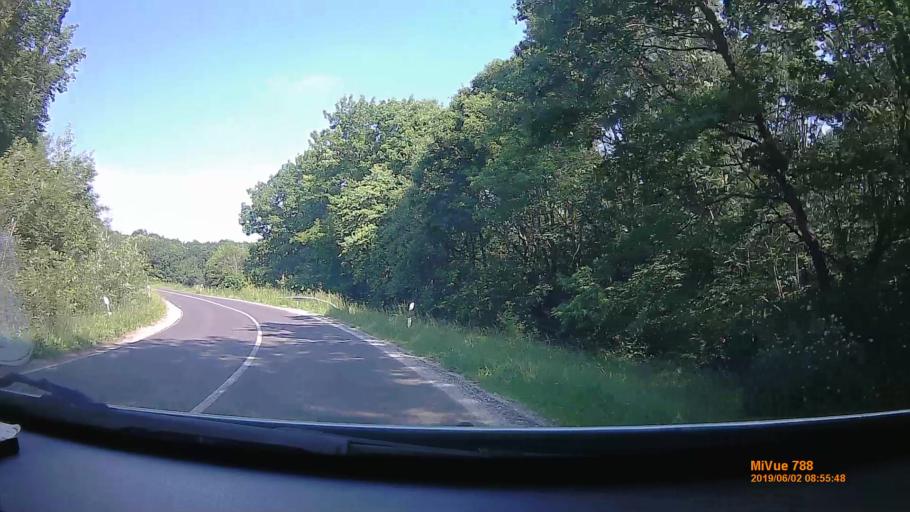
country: HU
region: Borsod-Abauj-Zemplen
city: Sajobabony
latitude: 48.1559
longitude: 20.6588
